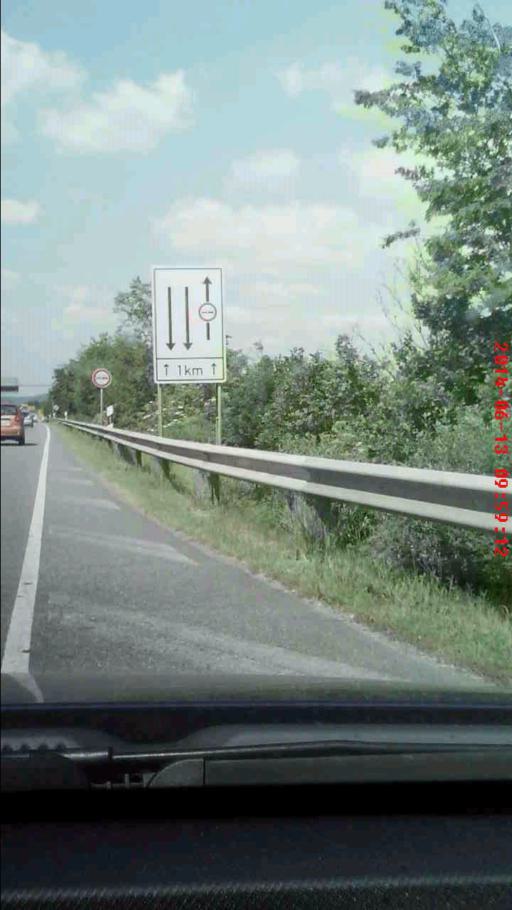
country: DE
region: Bavaria
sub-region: Upper Palatinate
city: Cham
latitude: 49.2143
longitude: 12.6990
